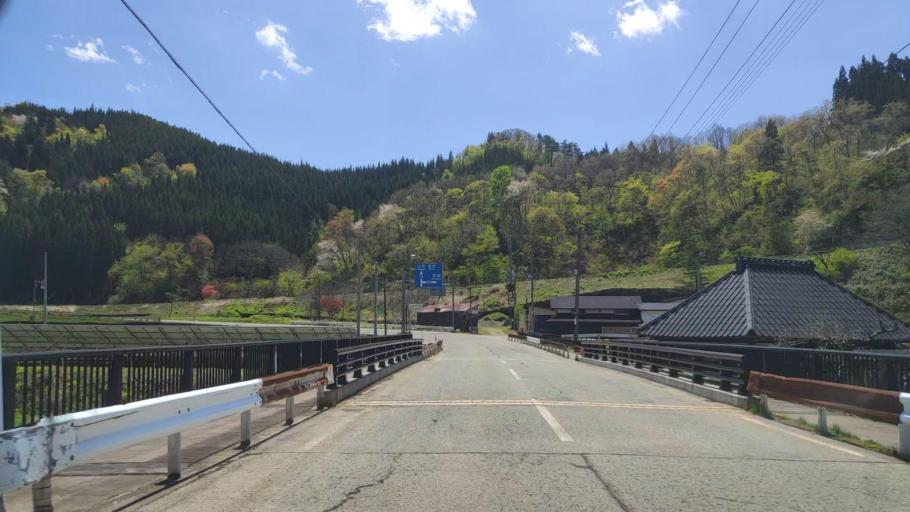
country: JP
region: Yamagata
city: Shinjo
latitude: 38.9209
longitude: 140.3334
